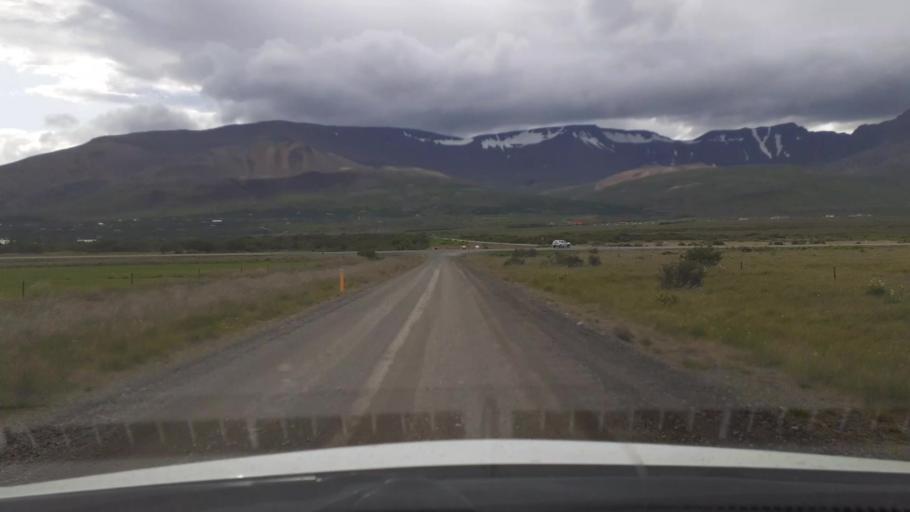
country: IS
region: West
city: Borgarnes
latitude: 64.5446
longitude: -21.6197
